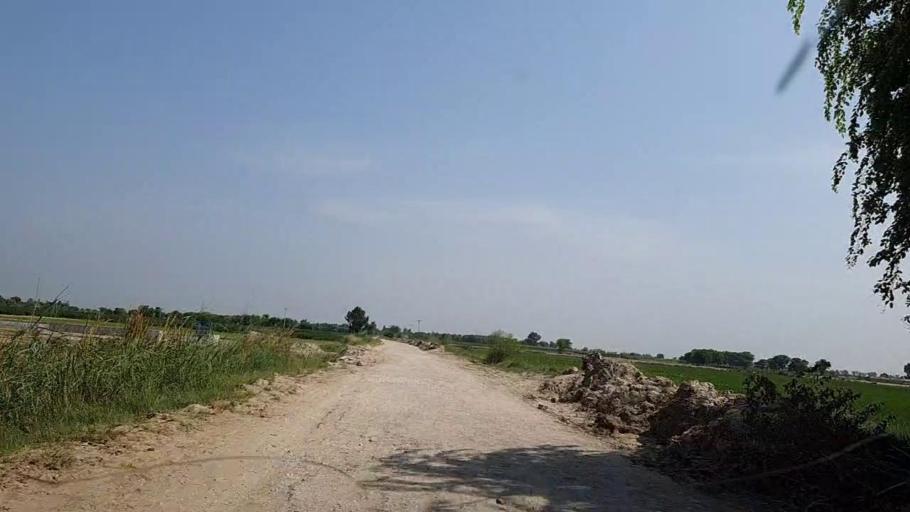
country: PK
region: Sindh
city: Khanpur
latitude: 27.7924
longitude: 69.3166
